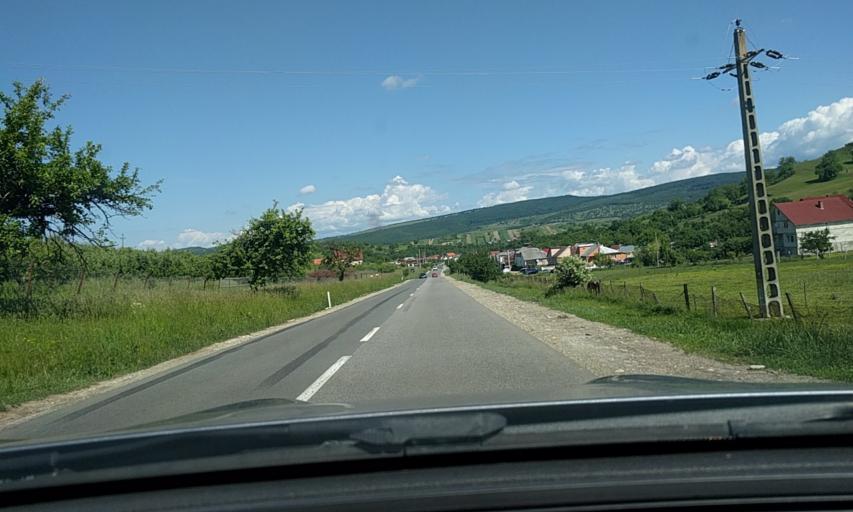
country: RO
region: Bistrita-Nasaud
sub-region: Comuna Dumitra
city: Dumitra
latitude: 47.2098
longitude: 24.4709
